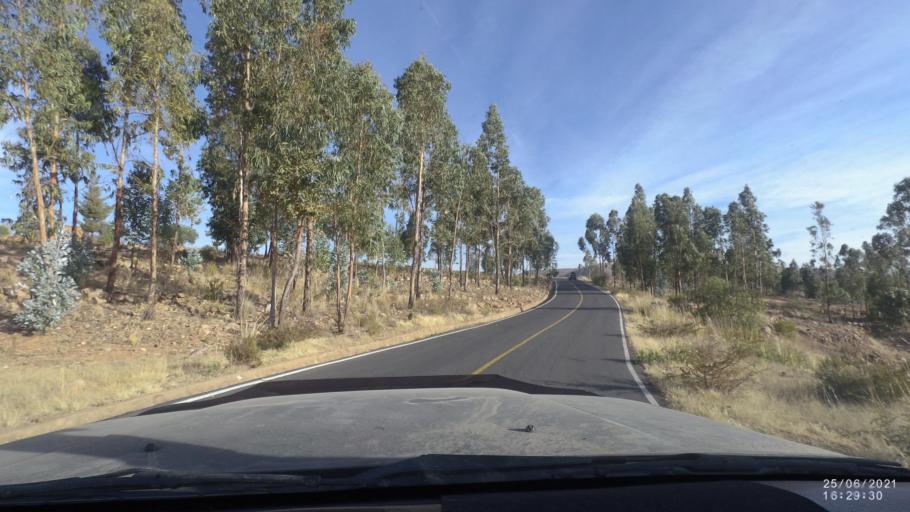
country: BO
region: Cochabamba
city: Arani
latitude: -17.7843
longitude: -65.8091
